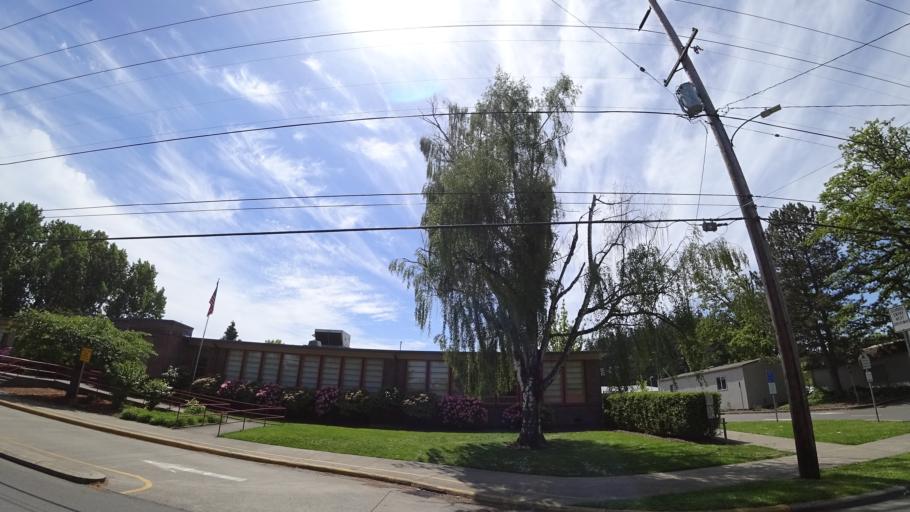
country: US
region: Oregon
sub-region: Washington County
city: Aloha
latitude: 45.4914
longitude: -122.8602
